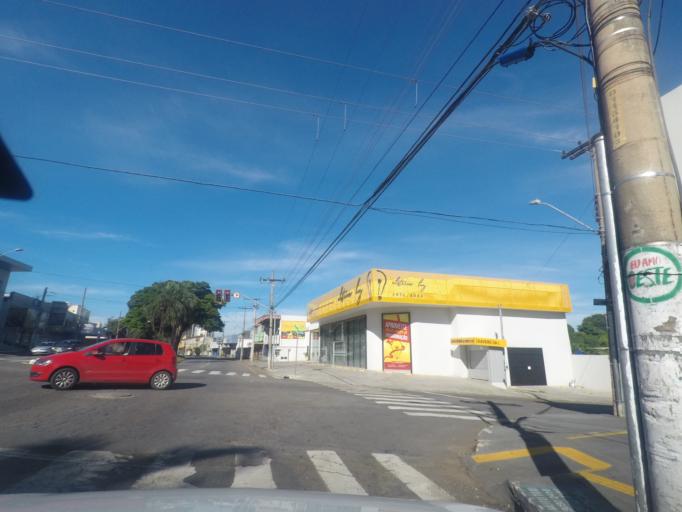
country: BR
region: Goias
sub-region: Goiania
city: Goiania
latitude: -16.6681
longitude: -49.2730
